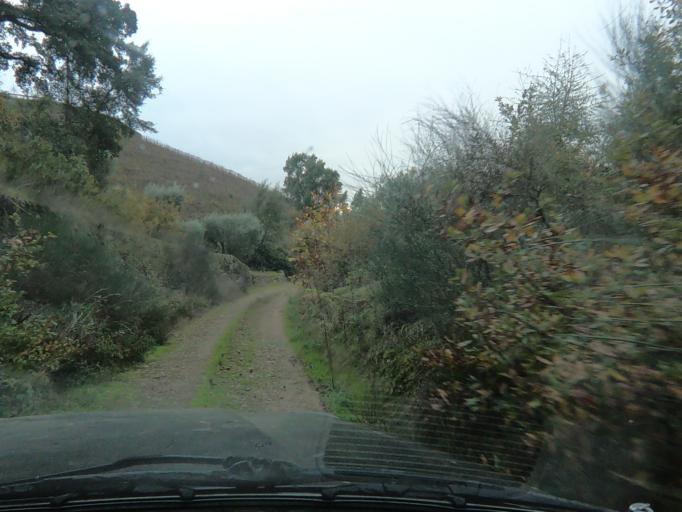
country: PT
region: Vila Real
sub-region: Santa Marta de Penaguiao
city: Santa Marta de Penaguiao
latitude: 41.2083
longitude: -7.7595
